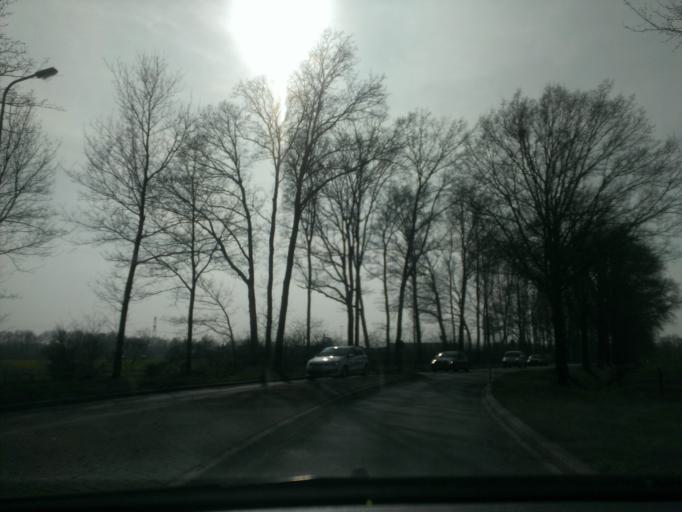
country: NL
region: Overijssel
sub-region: Gemeente Borne
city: Borne
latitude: 52.3027
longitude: 6.7347
